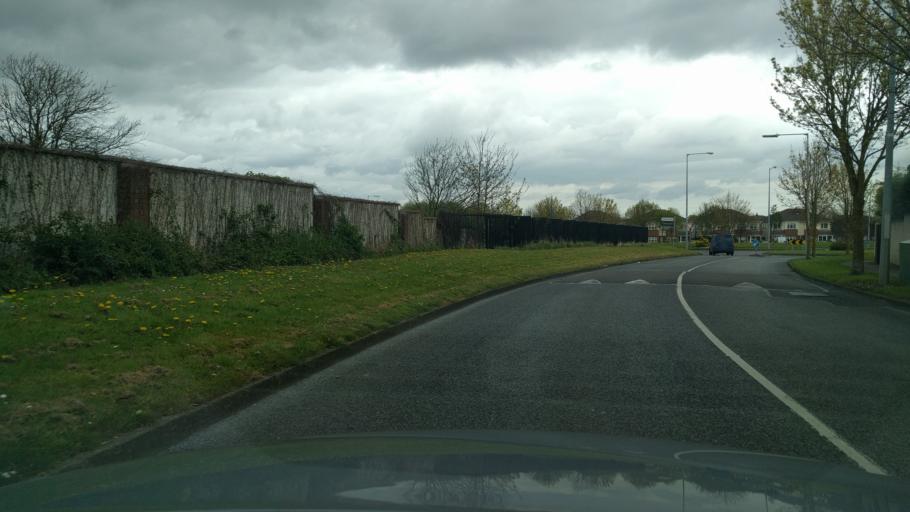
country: IE
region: Leinster
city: Tallaght
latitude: 53.3064
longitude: -6.3750
